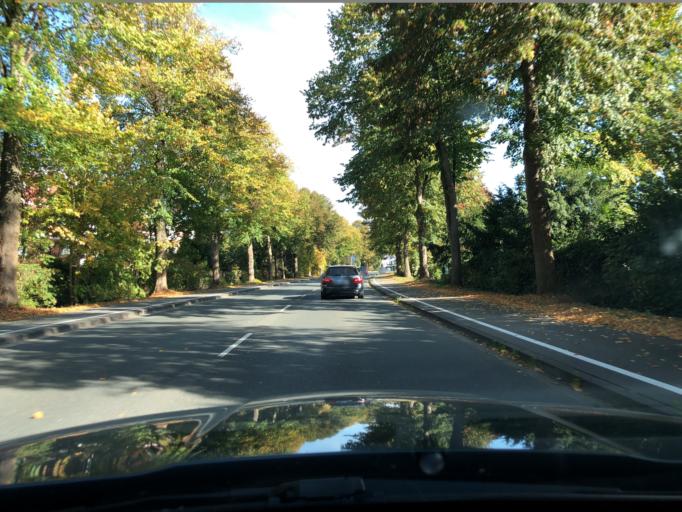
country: DE
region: North Rhine-Westphalia
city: Lengerich
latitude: 52.1842
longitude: 7.8561
